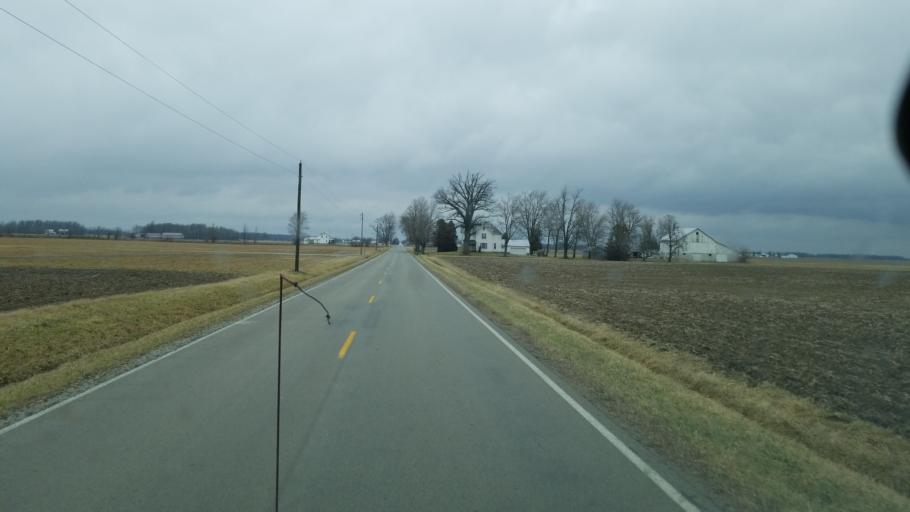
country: US
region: Ohio
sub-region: Hardin County
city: Forest
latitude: 40.7929
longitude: -83.4194
